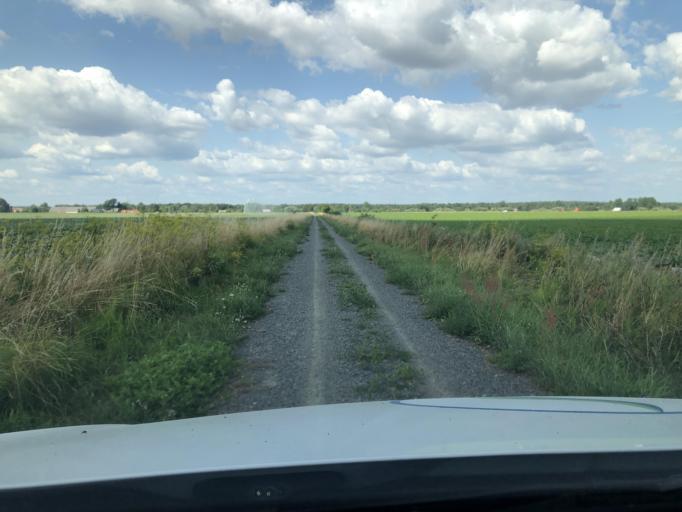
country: SE
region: Skane
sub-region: Kristianstads Kommun
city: Degeberga
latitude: 55.8884
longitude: 14.0809
